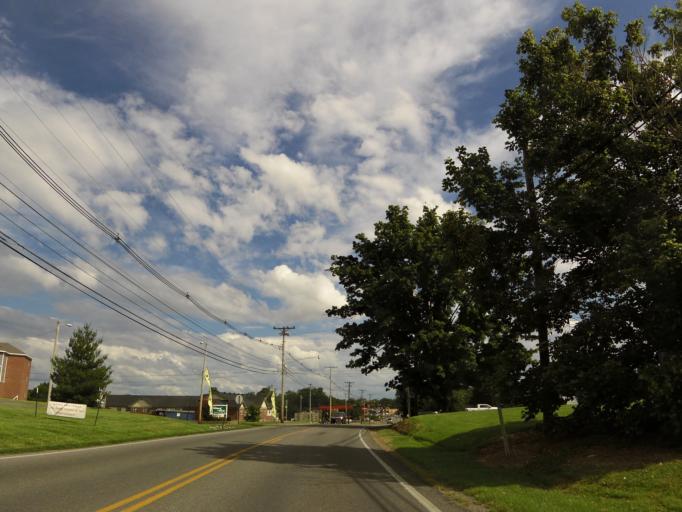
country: US
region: Kentucky
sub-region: Christian County
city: Hopkinsville
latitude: 36.8755
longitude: -87.5039
